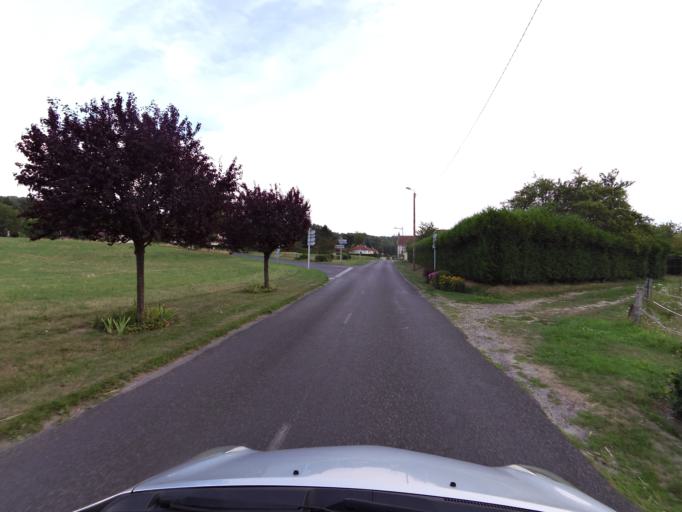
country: FR
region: Picardie
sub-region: Departement de l'Aisne
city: Bruyeres-et-Montberault
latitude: 49.5096
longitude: 3.6232
